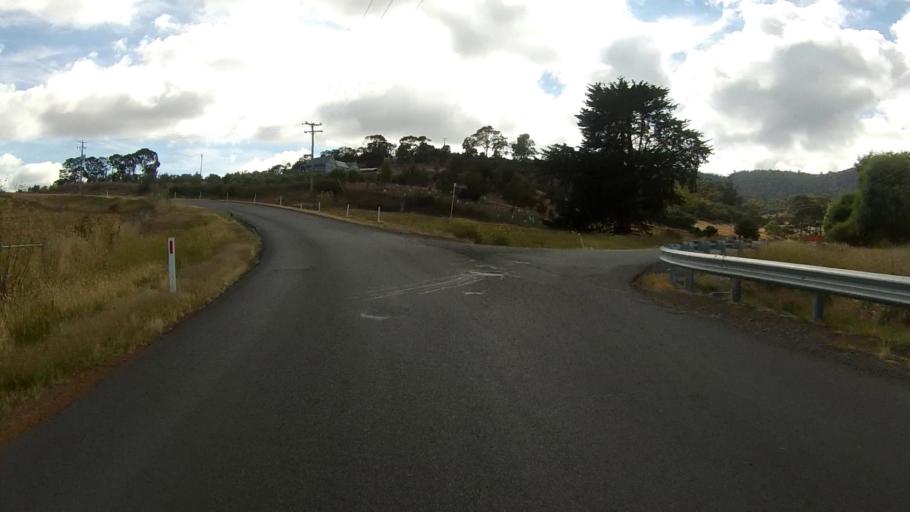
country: AU
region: Tasmania
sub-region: Brighton
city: Old Beach
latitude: -42.7591
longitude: 147.3039
